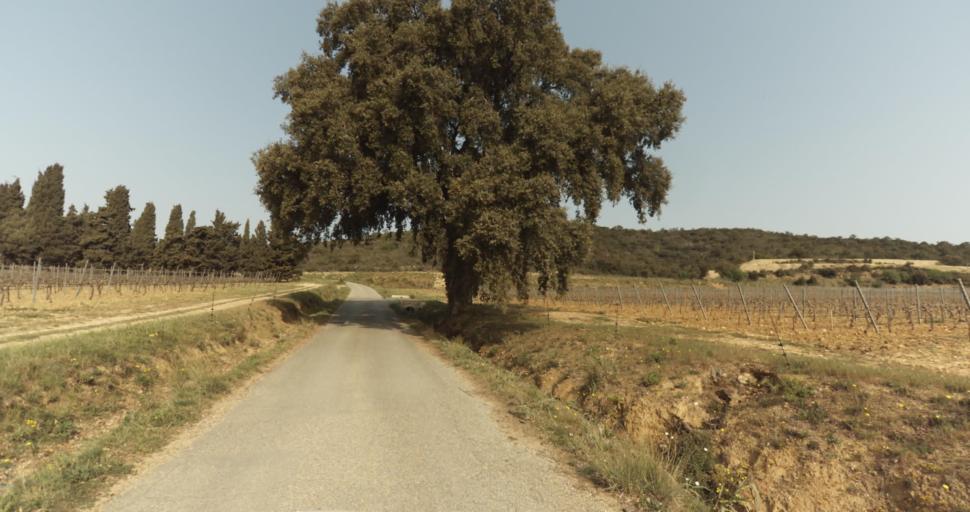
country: FR
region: Provence-Alpes-Cote d'Azur
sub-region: Departement du Var
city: Bormes-les-Mimosas
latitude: 43.1441
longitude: 6.3100
